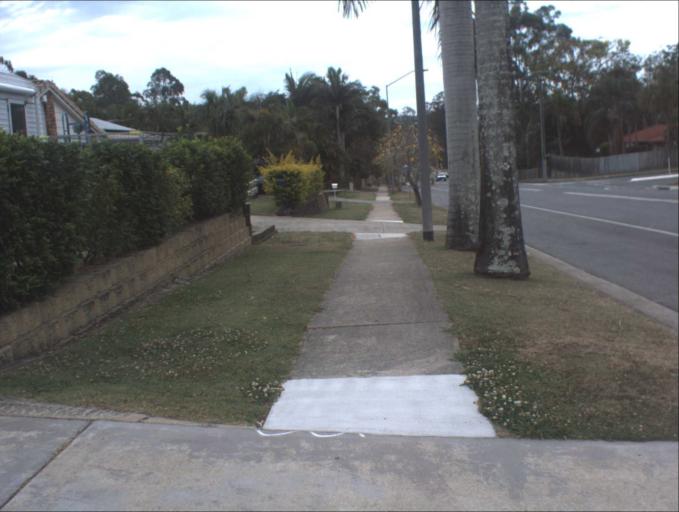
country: AU
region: Queensland
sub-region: Logan
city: Beenleigh
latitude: -27.6773
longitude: 153.1810
